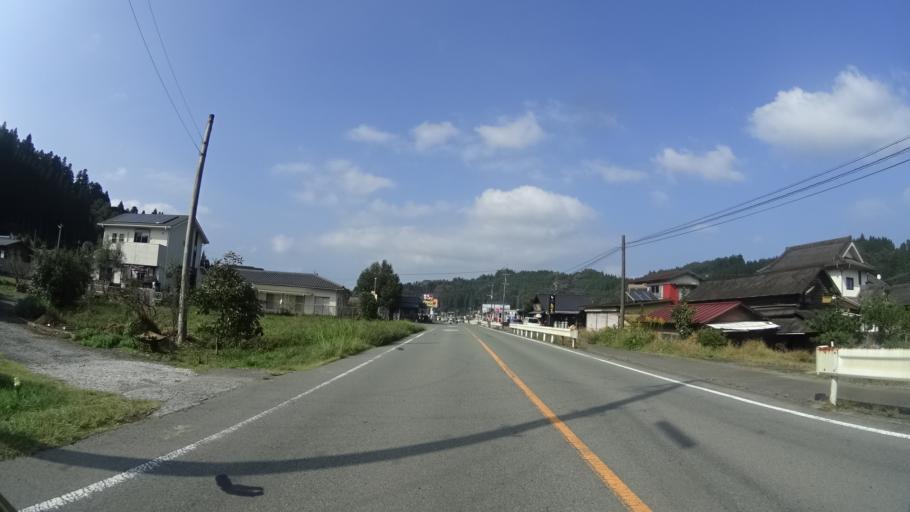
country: JP
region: Kumamoto
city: Aso
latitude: 33.1025
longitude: 131.0677
